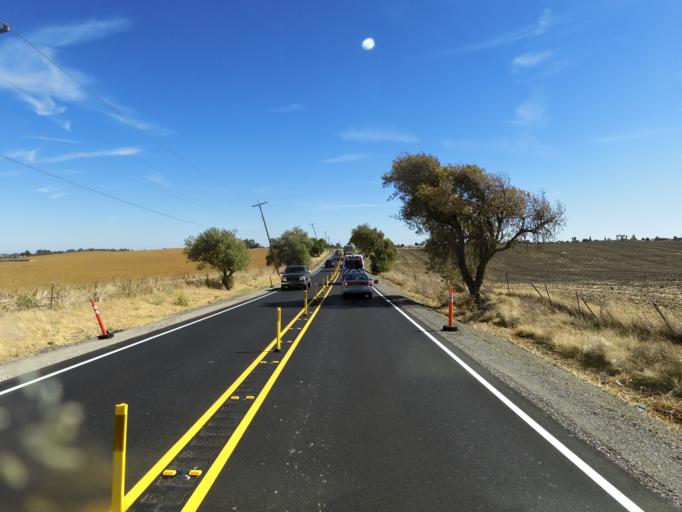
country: US
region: California
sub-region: Solano County
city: Rio Vista
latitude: 38.1690
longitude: -121.7073
